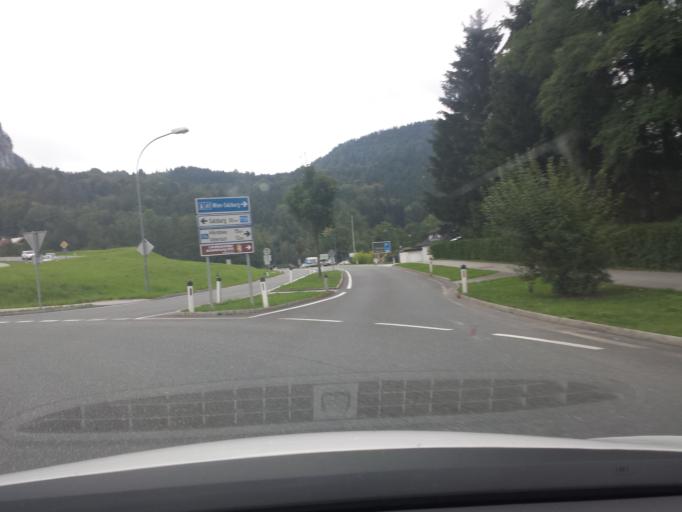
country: AT
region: Salzburg
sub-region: Politischer Bezirk Salzburg-Umgebung
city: Sankt Gilgen
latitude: 47.7699
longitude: 13.3604
